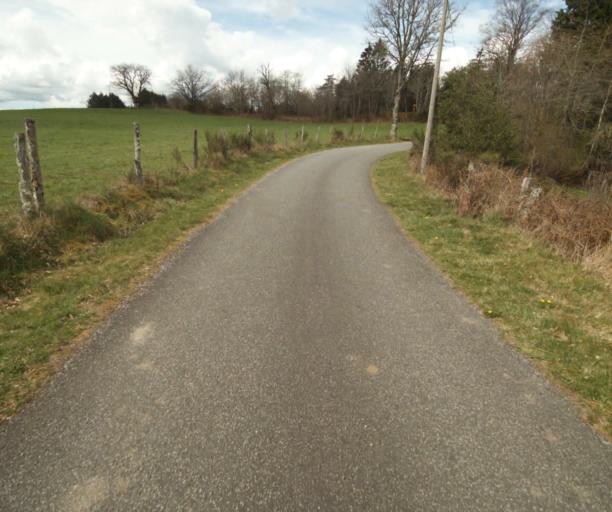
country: FR
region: Limousin
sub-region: Departement de la Correze
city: Correze
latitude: 45.3474
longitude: 1.9377
